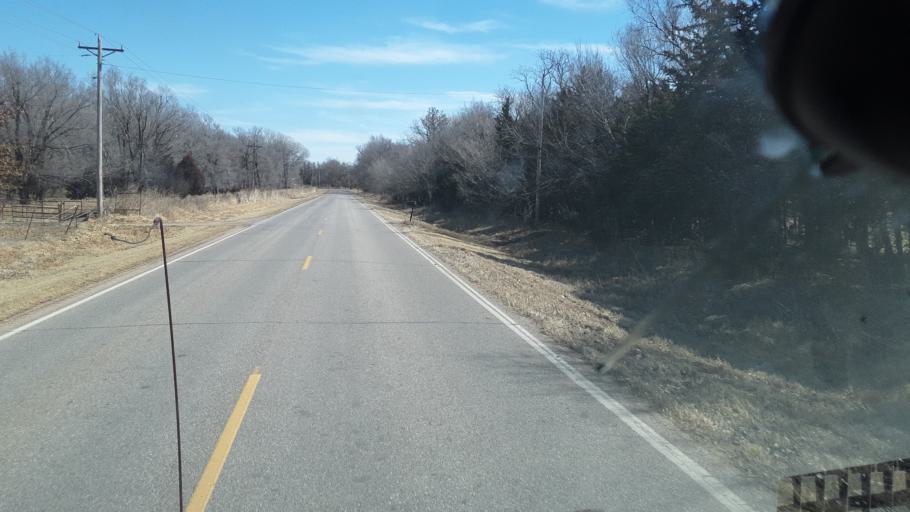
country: US
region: Kansas
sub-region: Reno County
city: Buhler
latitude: 38.1593
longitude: -97.8534
